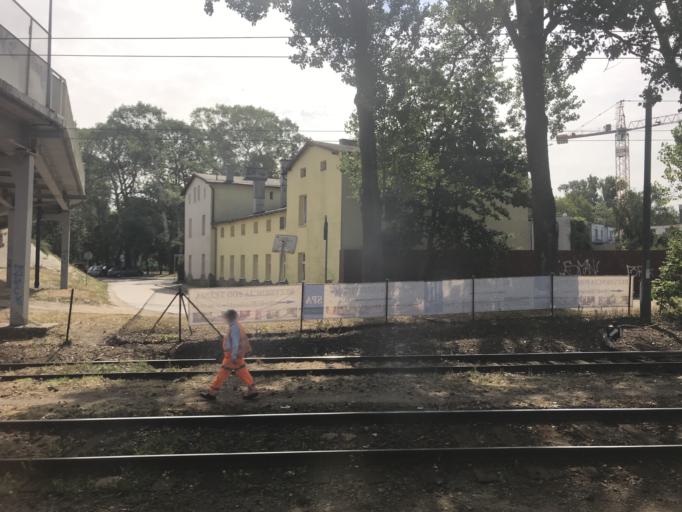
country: PL
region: Kujawsko-Pomorskie
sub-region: Powiat inowroclawski
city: Inowroclaw
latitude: 52.7971
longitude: 18.2355
